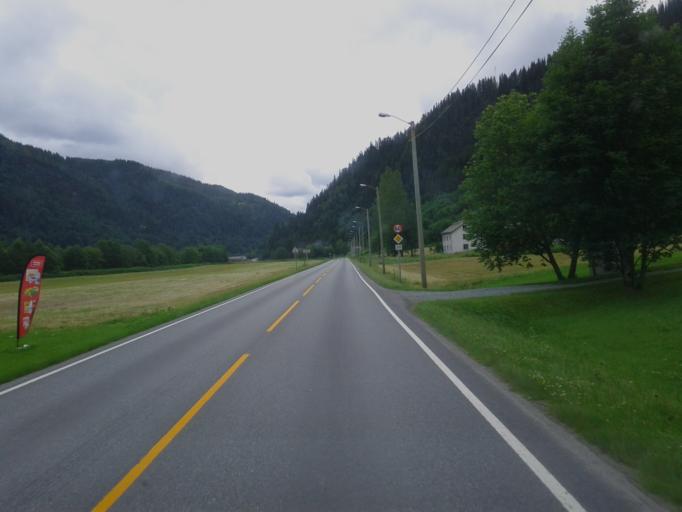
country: NO
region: Sor-Trondelag
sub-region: Midtre Gauldal
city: Storen
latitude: 62.9726
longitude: 10.5617
